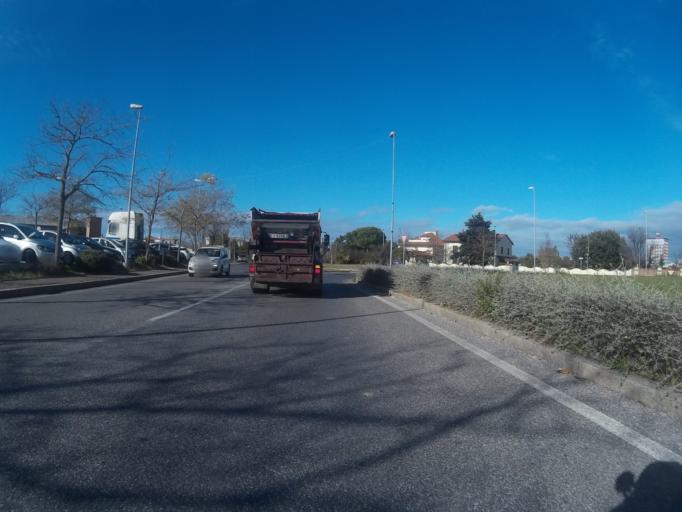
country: IT
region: Tuscany
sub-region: Provincia di Livorno
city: Livorno
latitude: 43.5526
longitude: 10.3411
